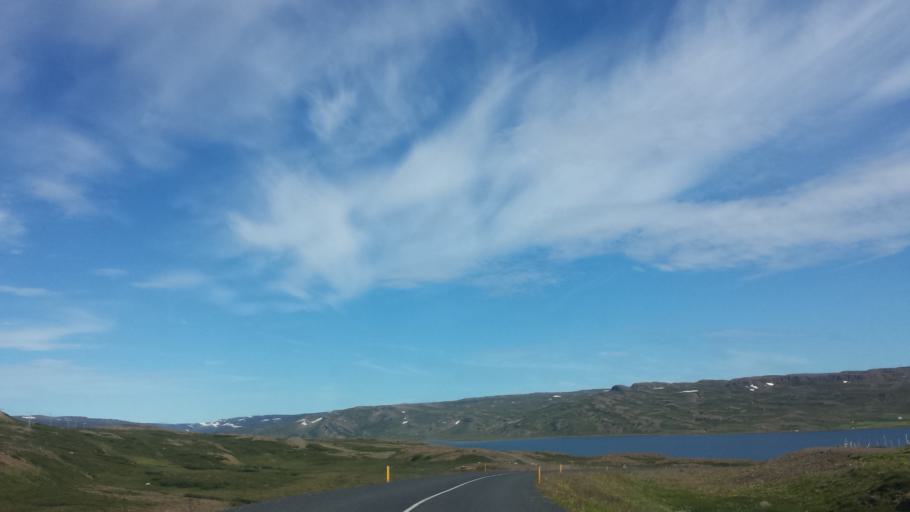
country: IS
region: West
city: Stykkisholmur
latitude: 65.7422
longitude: -21.7089
